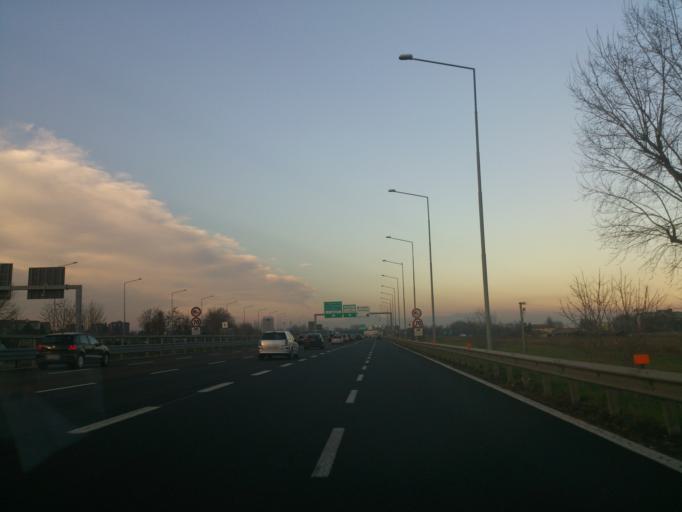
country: IT
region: Lombardy
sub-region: Citta metropolitana di Milano
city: Linate
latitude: 45.4391
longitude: 9.2570
